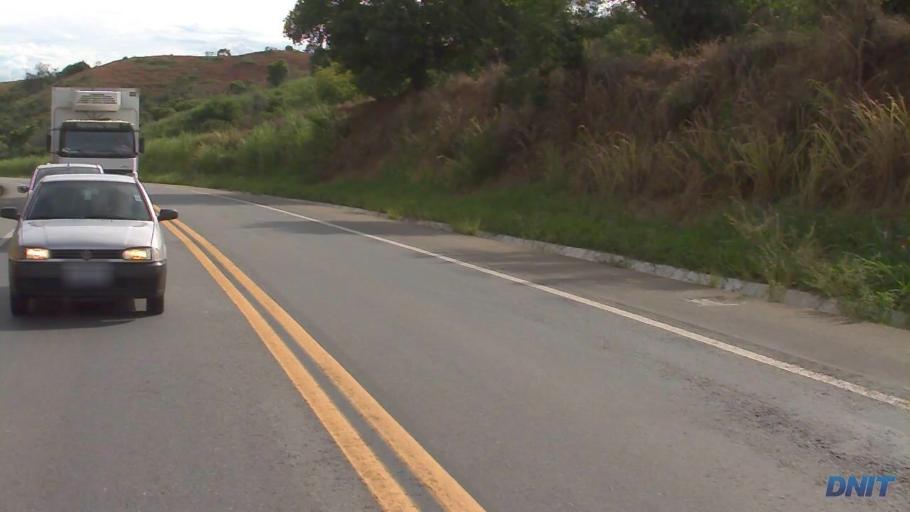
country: BR
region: Minas Gerais
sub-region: Belo Oriente
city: Belo Oriente
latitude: -19.2194
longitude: -42.3095
